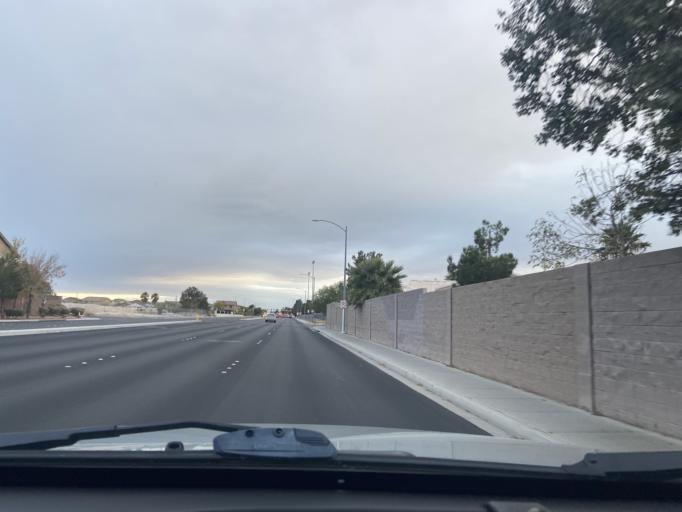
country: US
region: Nevada
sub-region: Clark County
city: North Las Vegas
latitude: 36.2365
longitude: -115.1803
